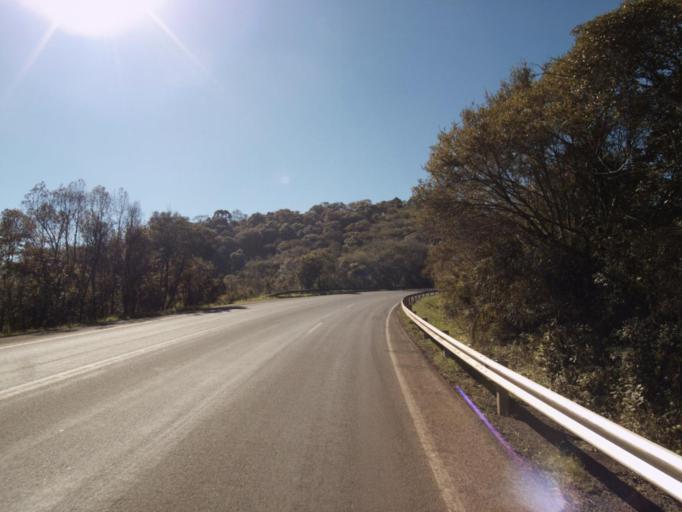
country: BR
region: Santa Catarina
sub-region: Sao Lourenco Do Oeste
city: Sao Lourenco dOeste
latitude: -26.8245
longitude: -53.1052
